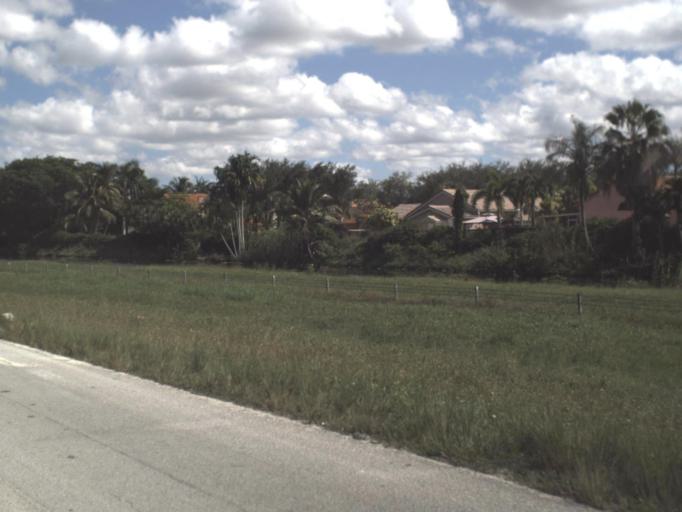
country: US
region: Florida
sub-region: Miami-Dade County
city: Palm Springs North
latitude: 25.9520
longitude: -80.3472
